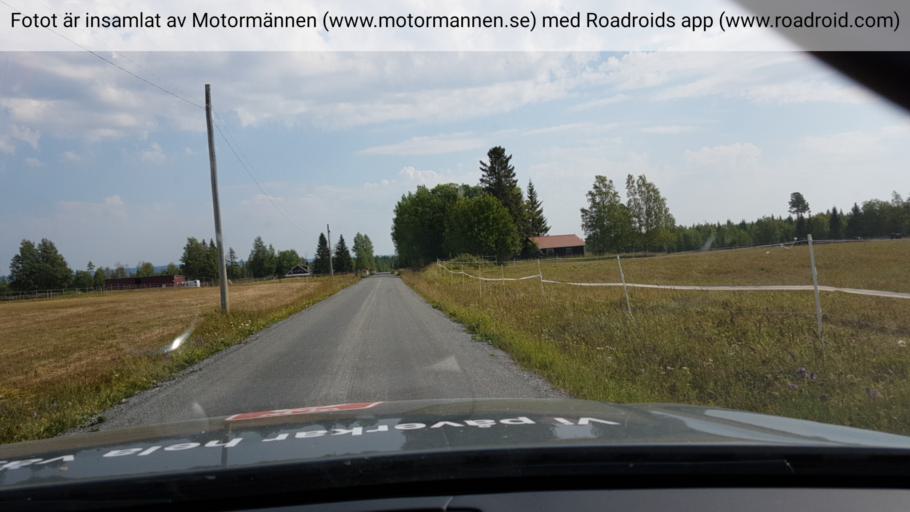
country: SE
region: Jaemtland
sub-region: OEstersunds Kommun
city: Ostersund
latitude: 63.1174
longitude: 14.6084
